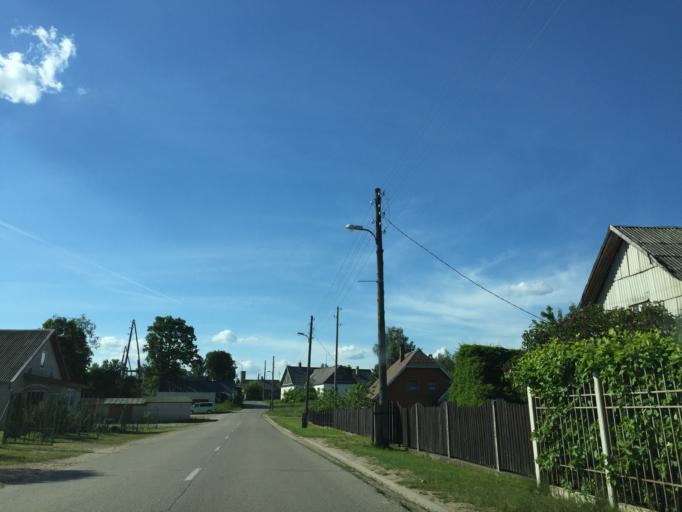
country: LV
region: Rezekne
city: Rezekne
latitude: 56.3460
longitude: 27.1664
